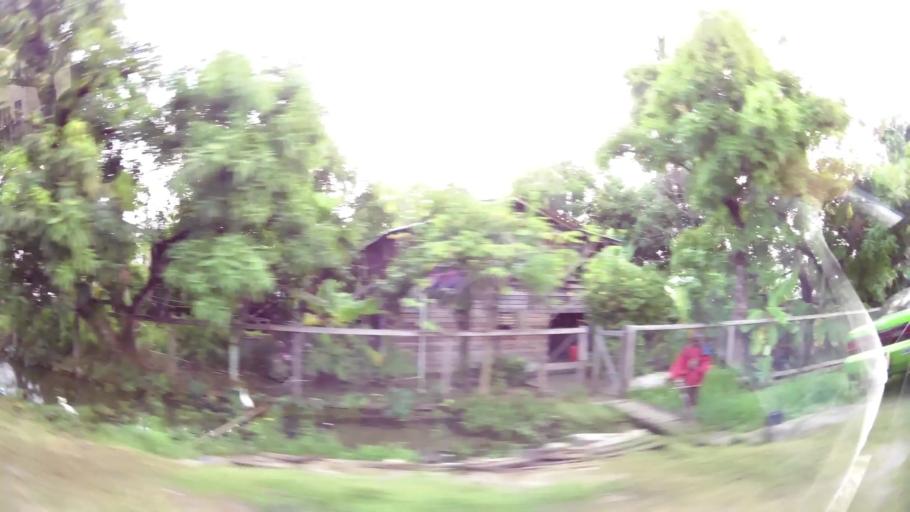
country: GY
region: Demerara-Mahaica
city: Georgetown
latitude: 6.7887
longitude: -58.0183
